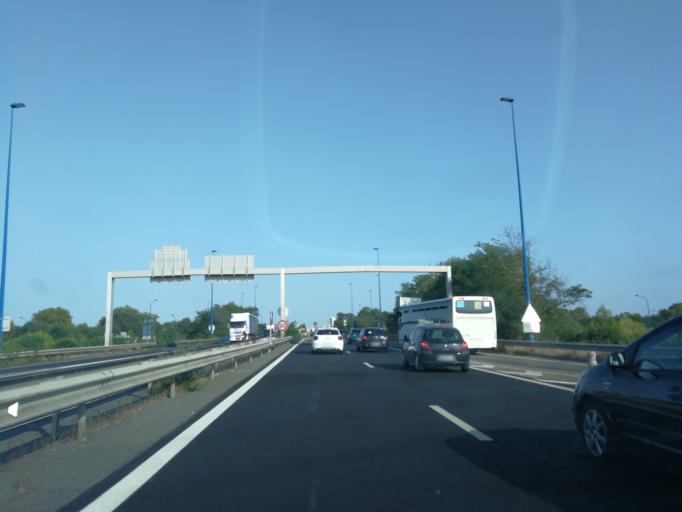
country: FR
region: Midi-Pyrenees
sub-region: Departement de la Haute-Garonne
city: Blagnac
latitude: 43.6244
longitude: 1.4163
